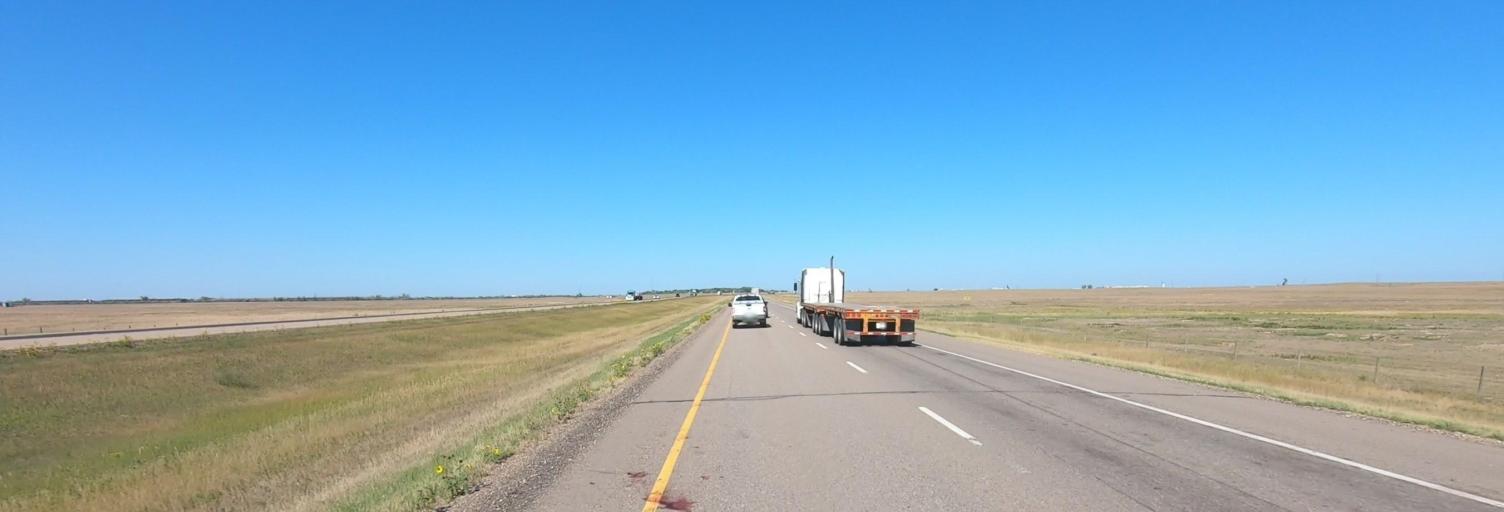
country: CA
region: Alberta
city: Brooks
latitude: 50.5262
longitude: -111.7710
